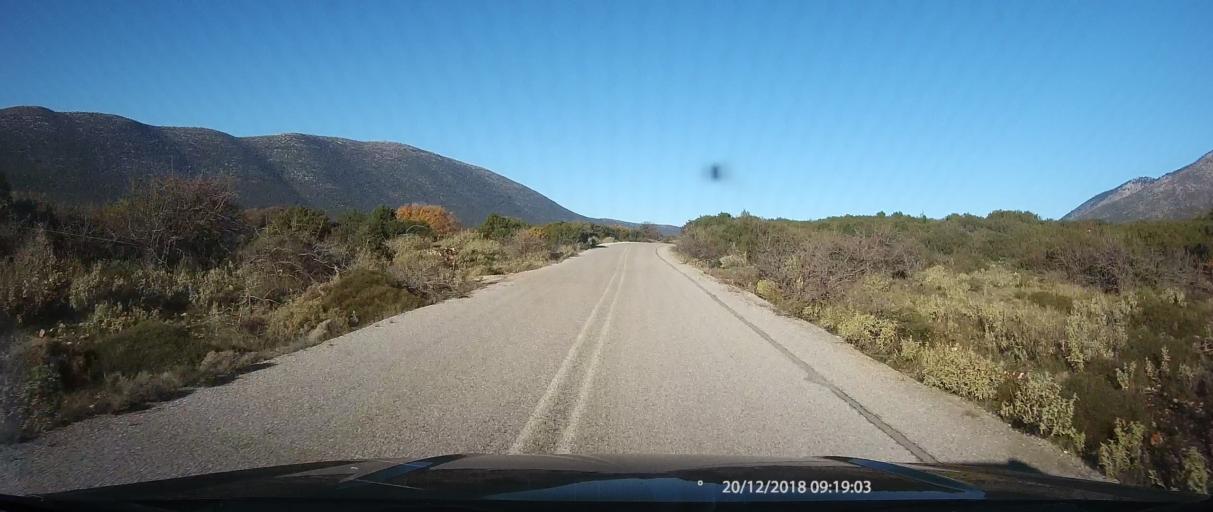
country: GR
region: Peloponnese
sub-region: Nomos Lakonias
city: Molaoi
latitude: 36.9155
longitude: 22.9459
